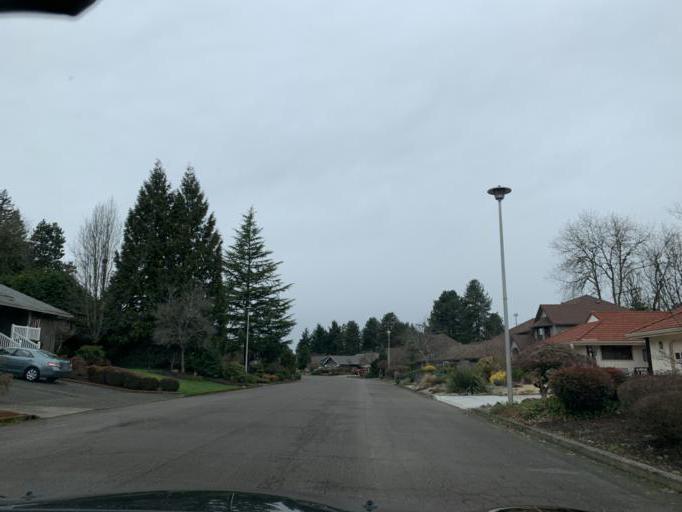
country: US
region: Washington
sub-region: Clark County
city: Walnut Grove
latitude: 45.6758
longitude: -122.5877
